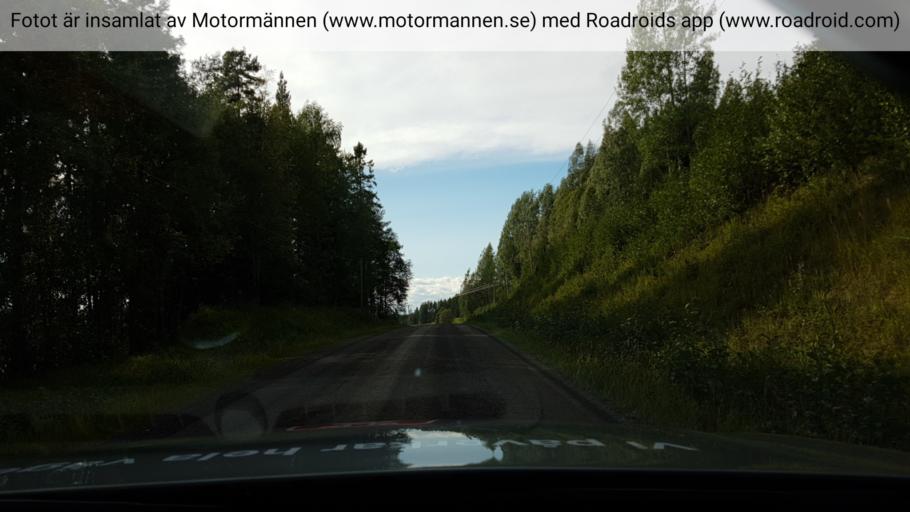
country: SE
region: Jaemtland
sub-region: Braecke Kommun
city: Braecke
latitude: 63.1964
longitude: 15.4834
